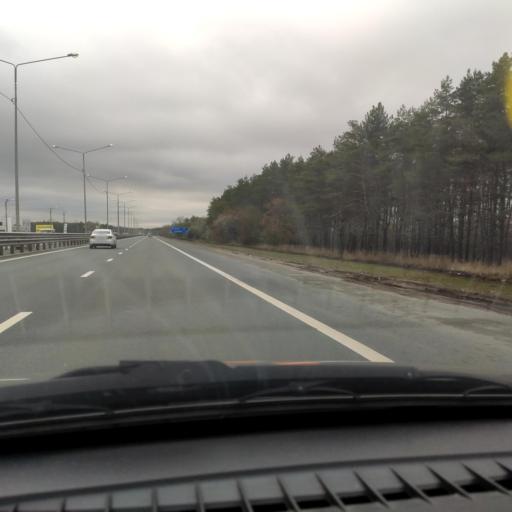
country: RU
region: Samara
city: Zhigulevsk
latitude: 53.5135
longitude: 49.5981
